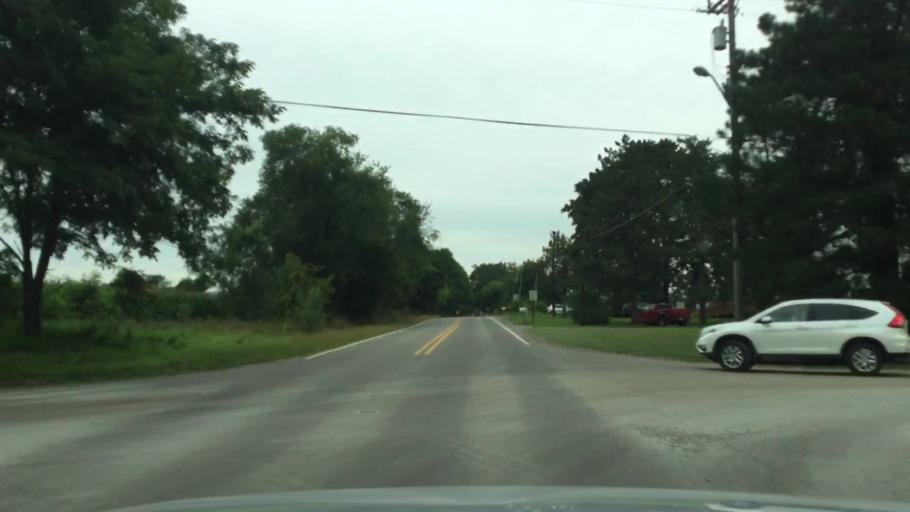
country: US
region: Michigan
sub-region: Washtenaw County
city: Ypsilanti
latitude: 42.1724
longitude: -83.6441
